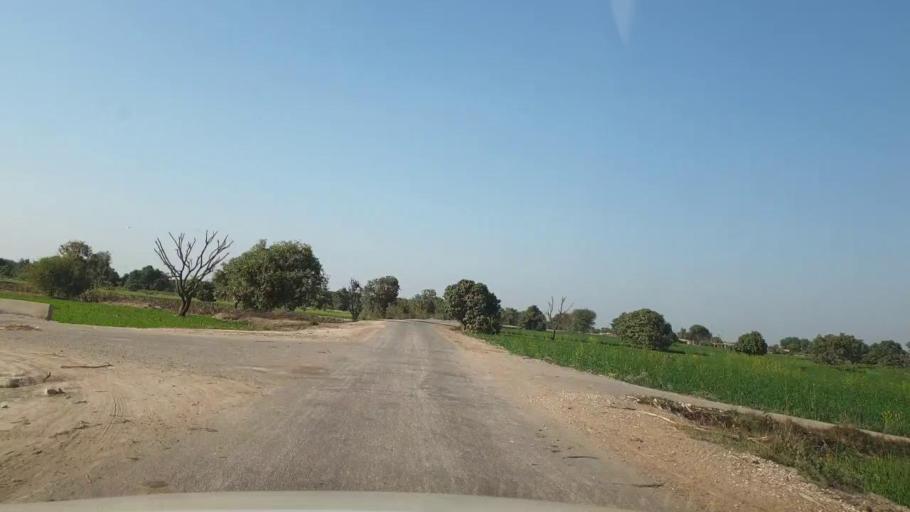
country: PK
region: Sindh
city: Tando Allahyar
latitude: 25.4954
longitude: 68.6531
